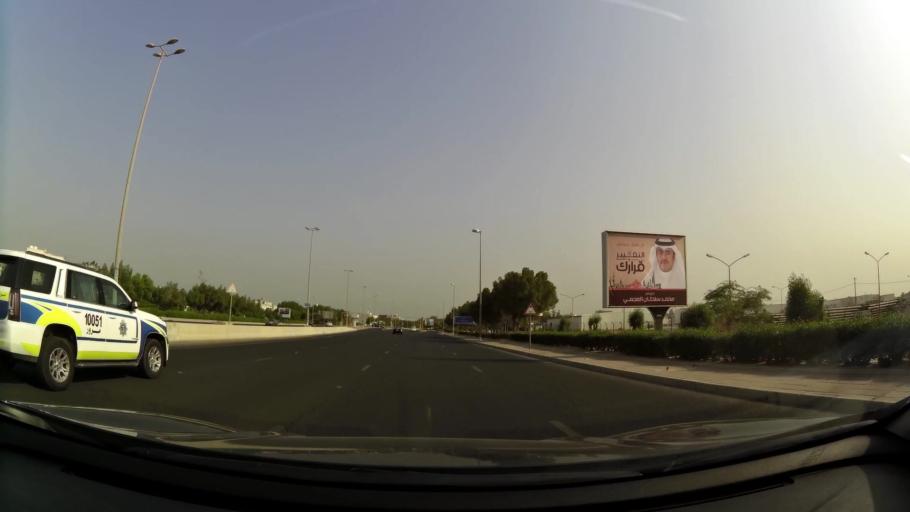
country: KW
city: Al Funaytis
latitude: 29.2269
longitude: 48.0794
